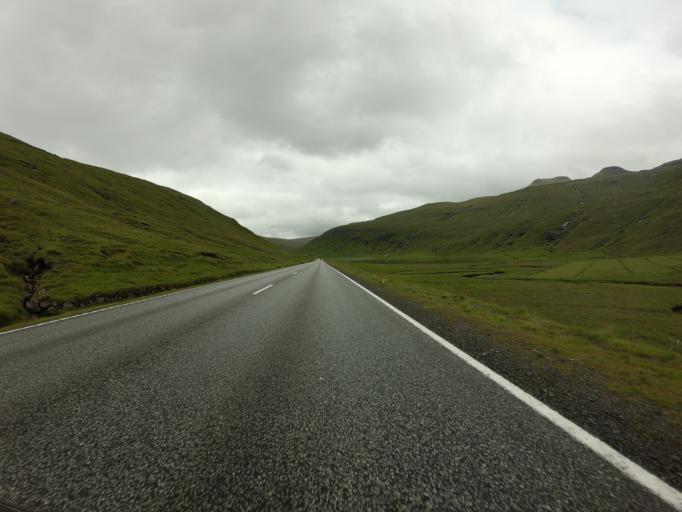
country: FO
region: Streymoy
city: Kollafjordhur
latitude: 62.1225
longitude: -6.9911
